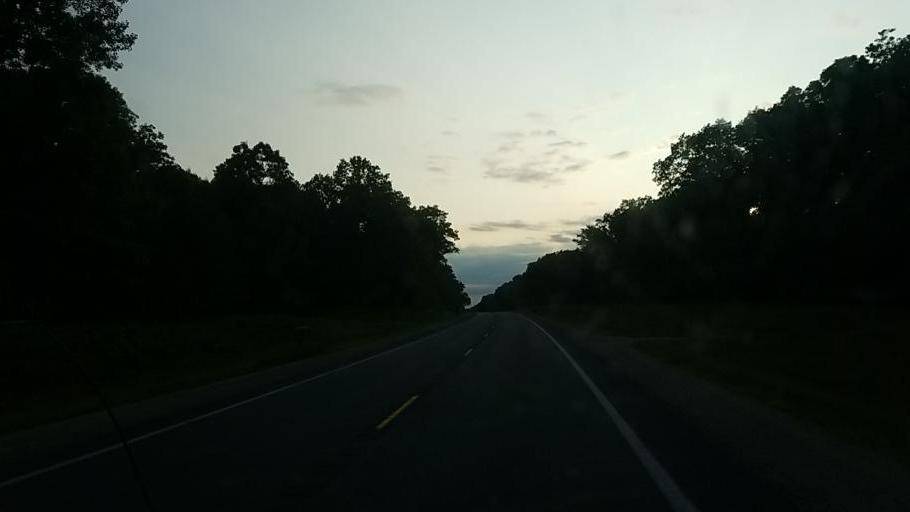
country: US
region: Michigan
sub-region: Newaygo County
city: Newaygo
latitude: 43.4064
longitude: -85.6847
